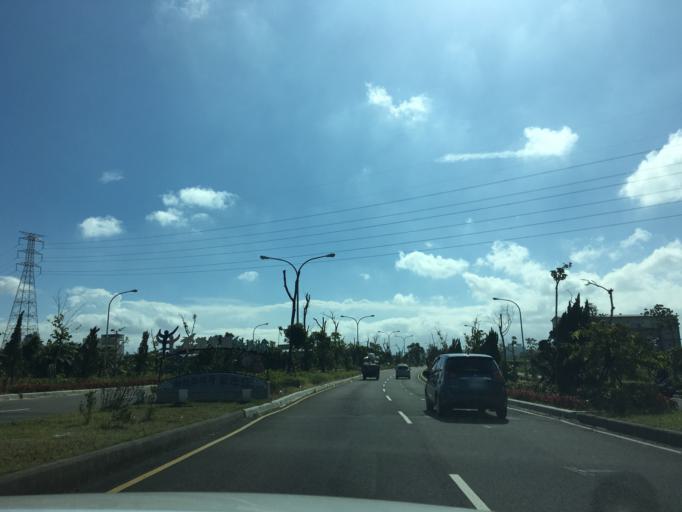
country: TW
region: Taiwan
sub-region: Hsinchu
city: Zhubei
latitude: 24.7934
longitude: 121.0217
